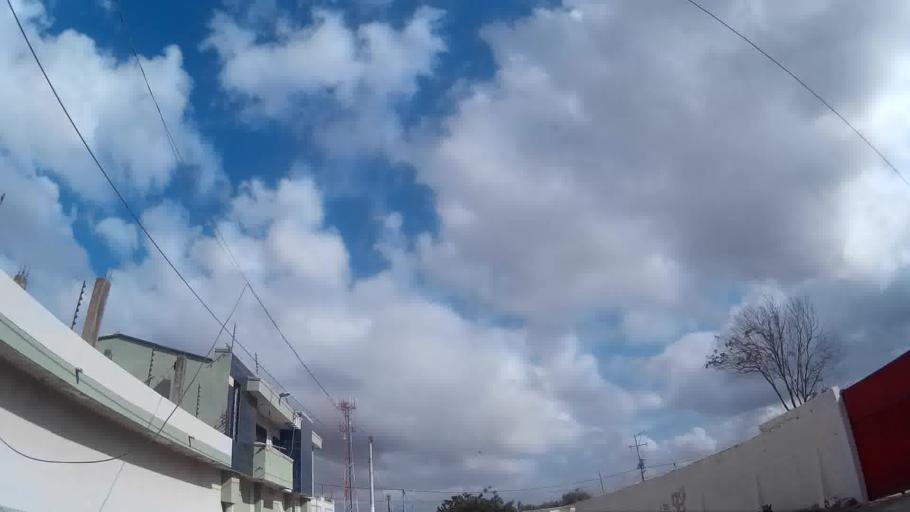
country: CO
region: La Guajira
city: Maicao
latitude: 11.3825
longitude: -72.2381
